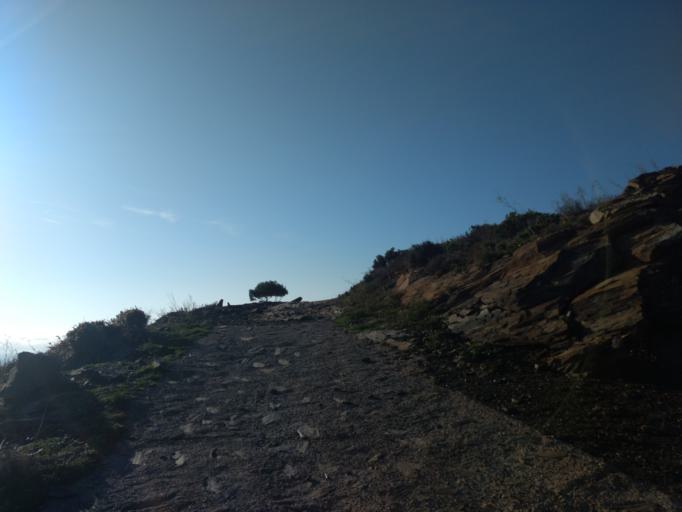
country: ES
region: Catalonia
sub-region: Provincia de Girona
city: Cadaques
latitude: 42.2775
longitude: 3.2784
